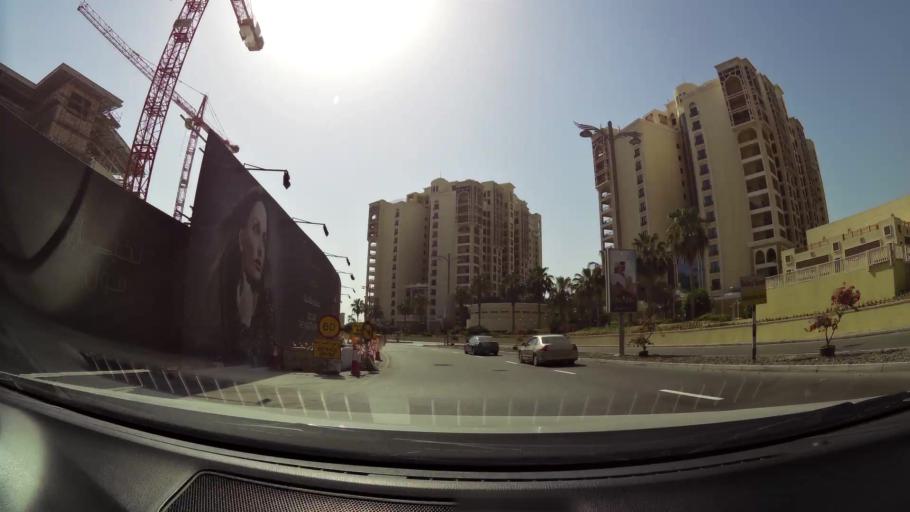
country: AE
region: Dubai
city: Dubai
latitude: 25.1147
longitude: 55.1393
